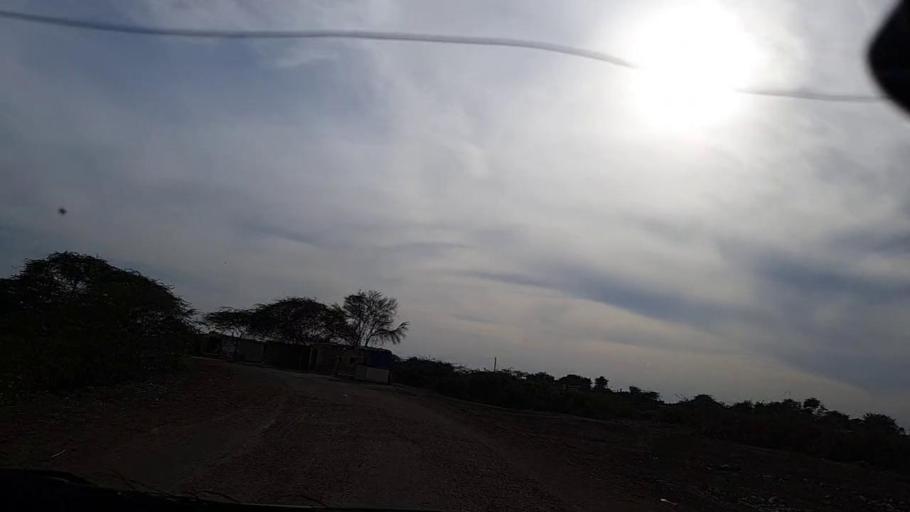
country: PK
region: Sindh
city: Dhoro Naro
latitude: 25.4129
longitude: 69.5188
